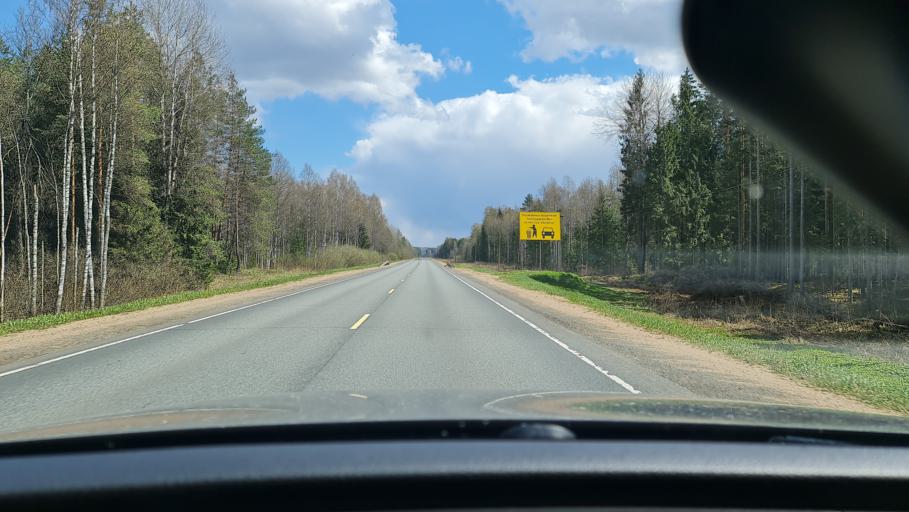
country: RU
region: Tverskaya
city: Zapadnaya Dvina
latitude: 56.3052
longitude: 32.1959
